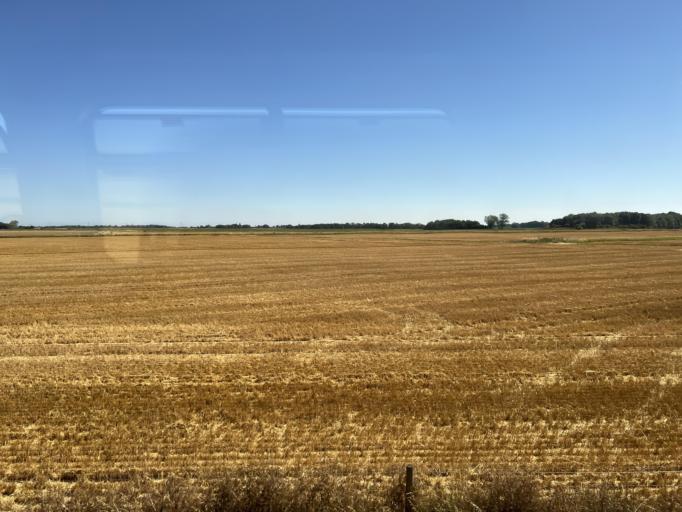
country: GB
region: England
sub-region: Lincolnshire
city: Spilsby
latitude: 53.1179
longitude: 0.1333
